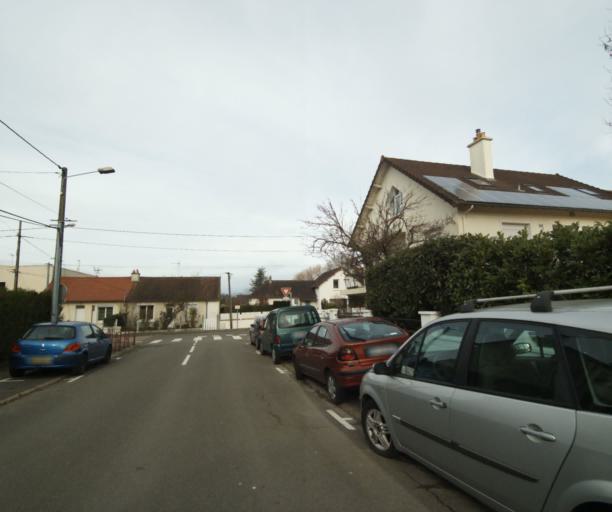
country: FR
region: Pays de la Loire
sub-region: Departement de la Sarthe
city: Coulaines
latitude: 48.0092
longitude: 0.2230
